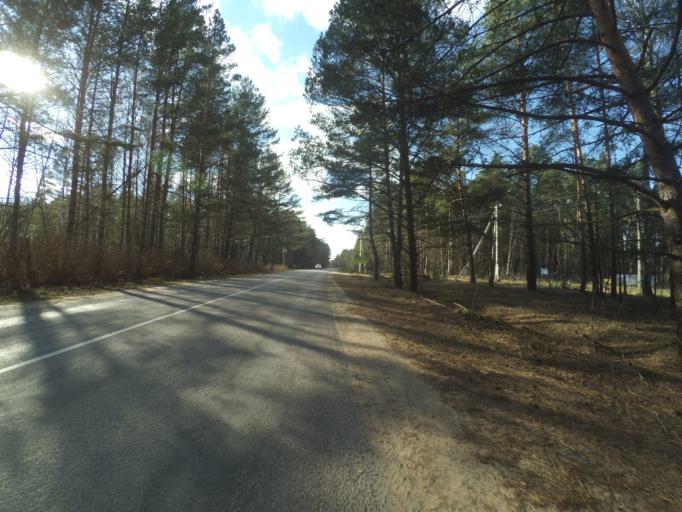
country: RU
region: Moskovskaya
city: Bol'shoye Gryzlovo
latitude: 54.8950
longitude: 37.7660
